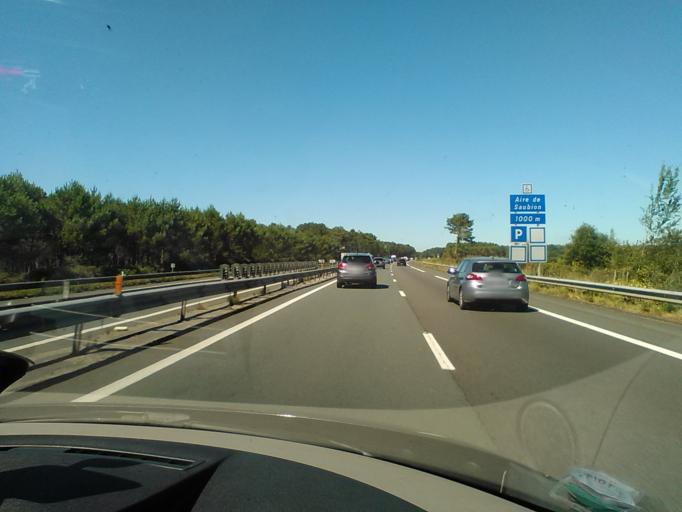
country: FR
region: Aquitaine
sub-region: Departement des Landes
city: Saint-Vincent-de-Tyrosse
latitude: 43.6812
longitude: -1.2876
